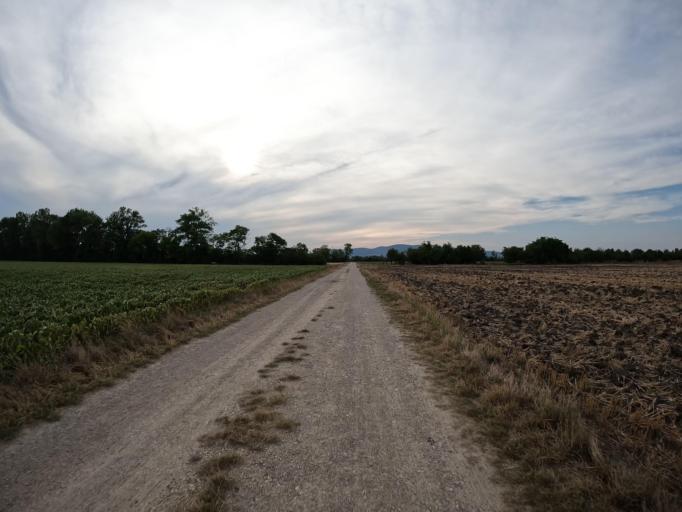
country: AT
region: Lower Austria
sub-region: Politischer Bezirk Baden
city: Trumau
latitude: 48.0024
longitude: 16.3381
